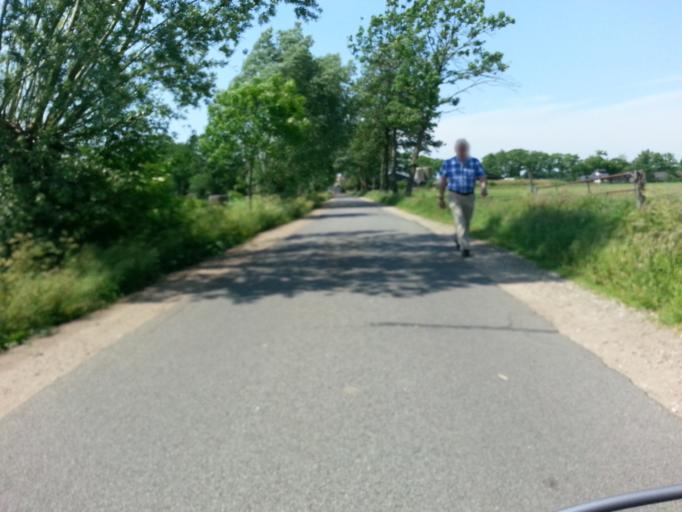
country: NL
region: Gelderland
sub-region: Gemeente Barneveld
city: Terschuur
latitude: 52.1433
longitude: 5.5008
